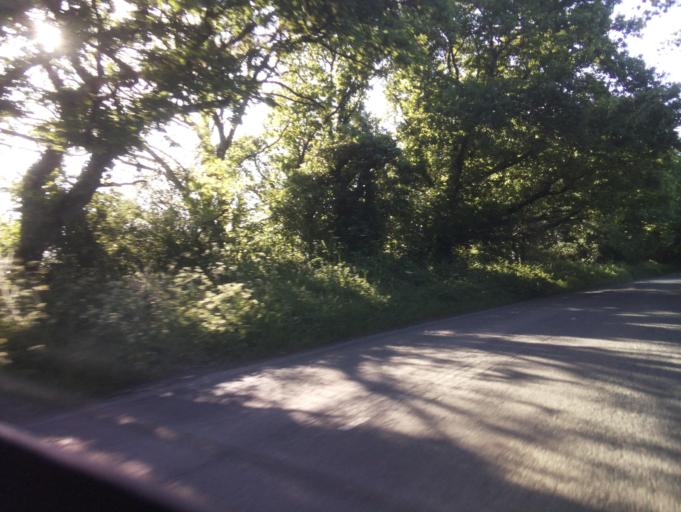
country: GB
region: England
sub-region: Devon
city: Axminster
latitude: 50.7460
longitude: -2.9885
